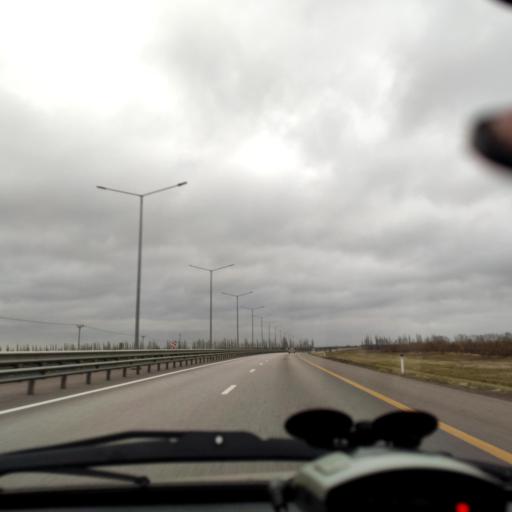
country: RU
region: Voronezj
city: Podkletnoye
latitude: 51.5889
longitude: 39.4307
